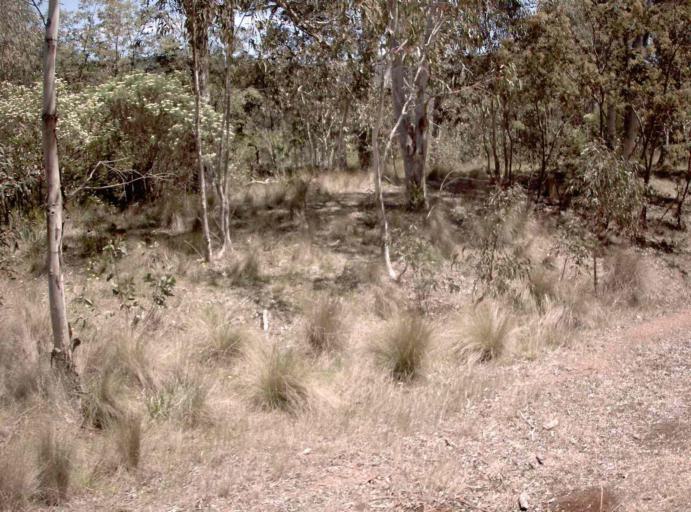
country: AU
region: New South Wales
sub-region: Snowy River
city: Jindabyne
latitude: -37.0770
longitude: 148.2604
